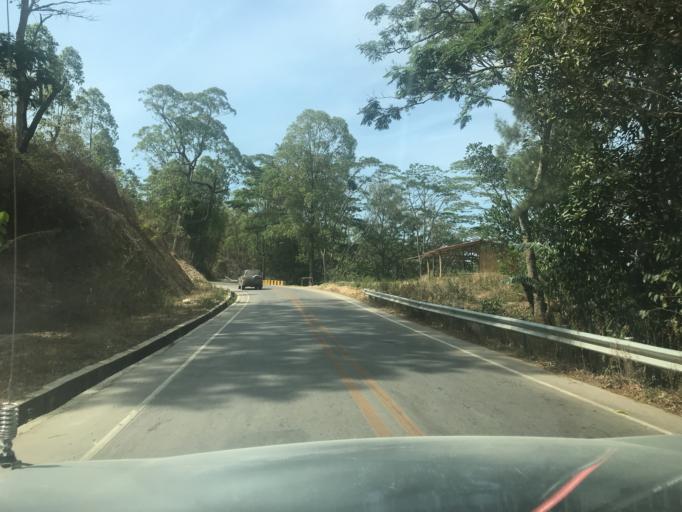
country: TL
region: Aileu
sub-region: Aileu Villa
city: Aileu
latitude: -8.6800
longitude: 125.5513
